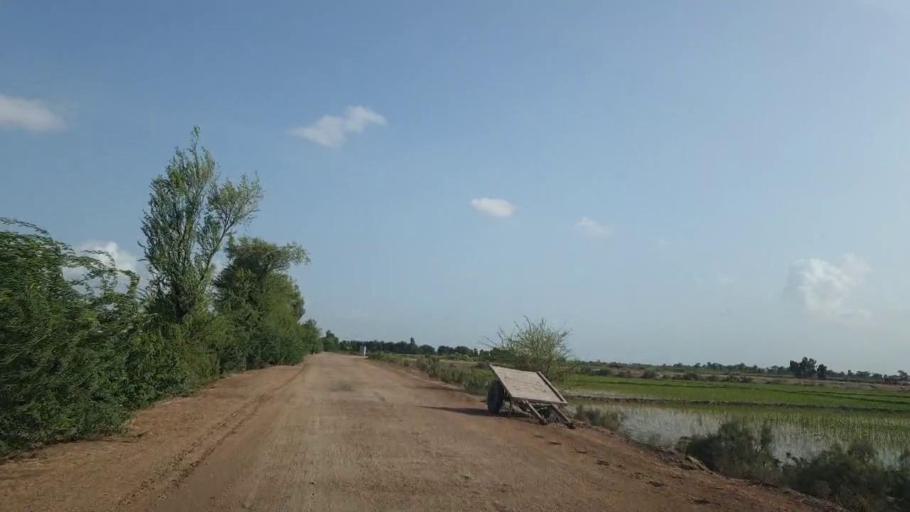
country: PK
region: Sindh
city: Kadhan
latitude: 24.6277
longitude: 69.0959
